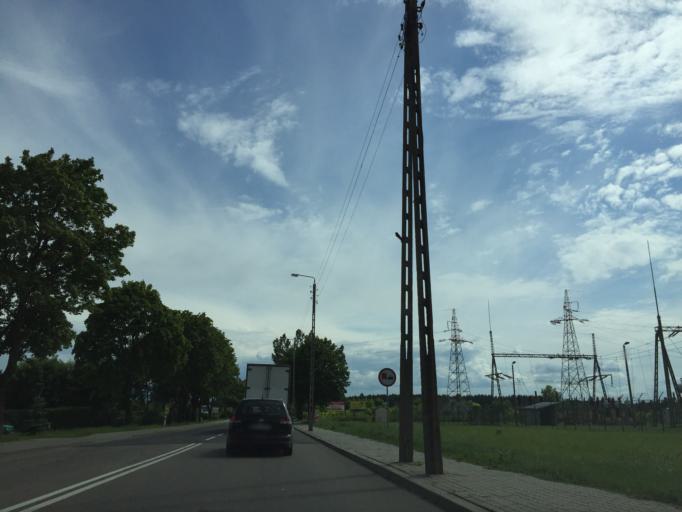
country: PL
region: Podlasie
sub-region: Powiat siemiatycki
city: Siemiatycze
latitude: 52.4053
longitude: 22.8712
